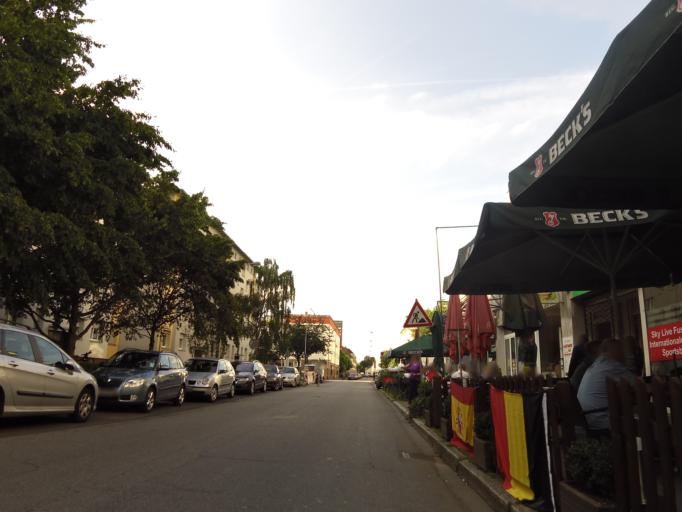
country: DE
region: Hesse
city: Niederrad
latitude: 50.0841
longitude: 8.6384
